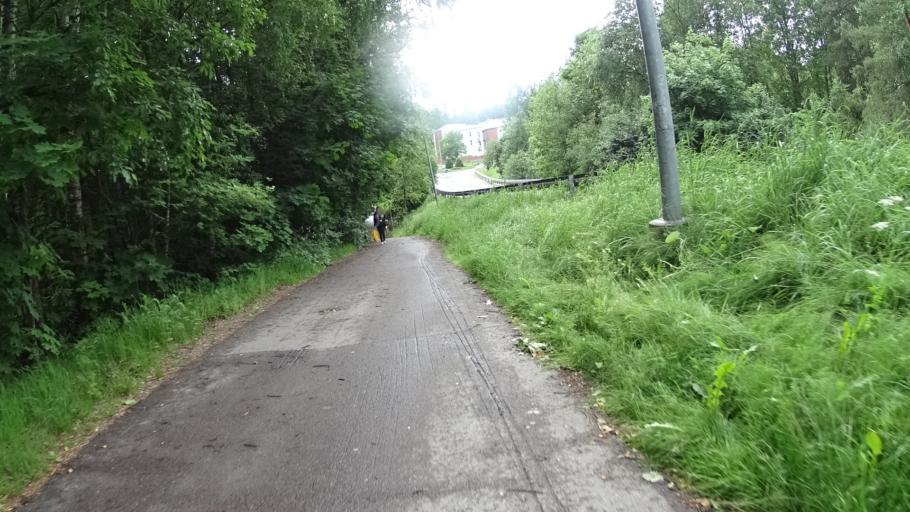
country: FI
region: Uusimaa
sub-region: Helsinki
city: Teekkarikylae
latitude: 60.2527
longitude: 24.8688
